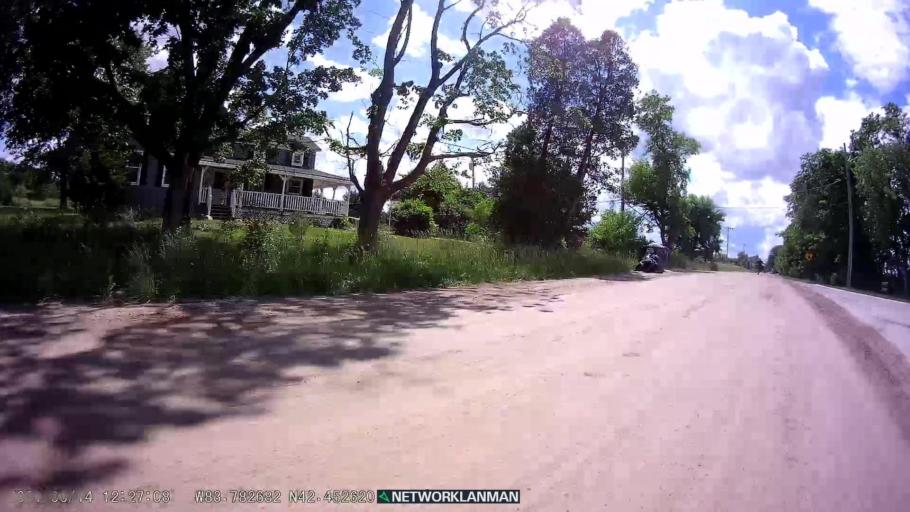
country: US
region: Michigan
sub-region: Livingston County
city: Whitmore Lake
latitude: 42.4527
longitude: -83.7830
